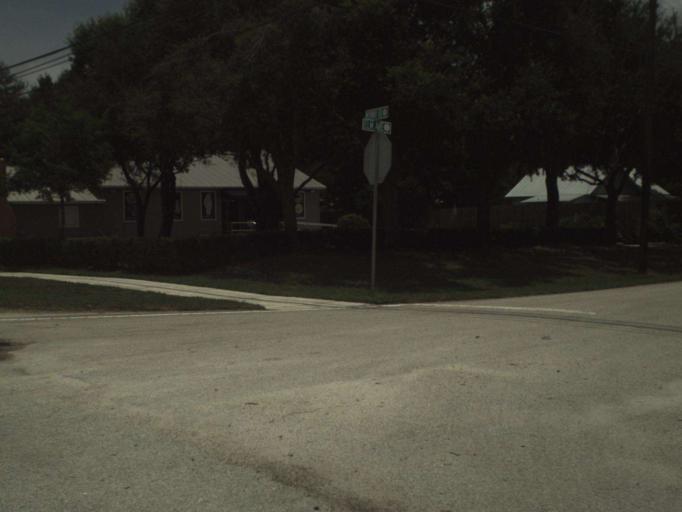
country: US
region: Florida
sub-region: Saint Lucie County
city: White City
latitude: 27.3743
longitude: -80.3359
